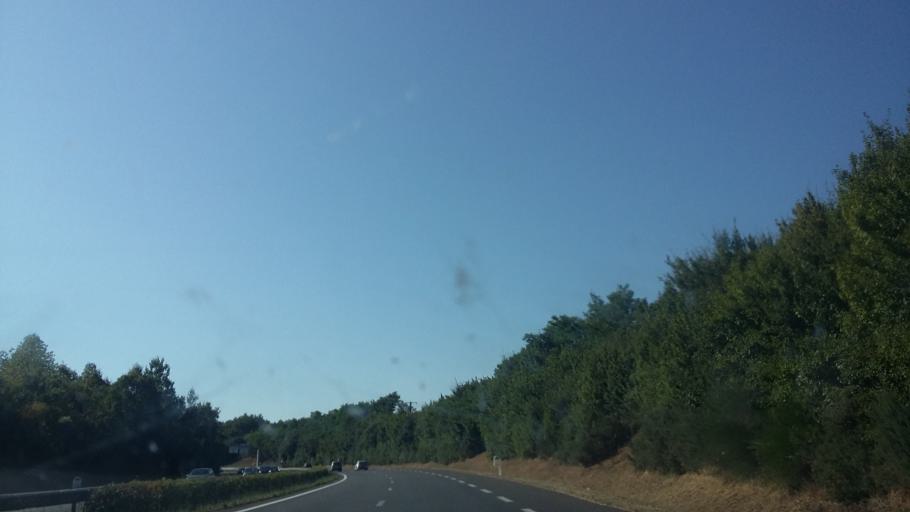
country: FR
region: Pays de la Loire
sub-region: Departement de la Vendee
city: Challans
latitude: 46.8609
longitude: -1.8576
